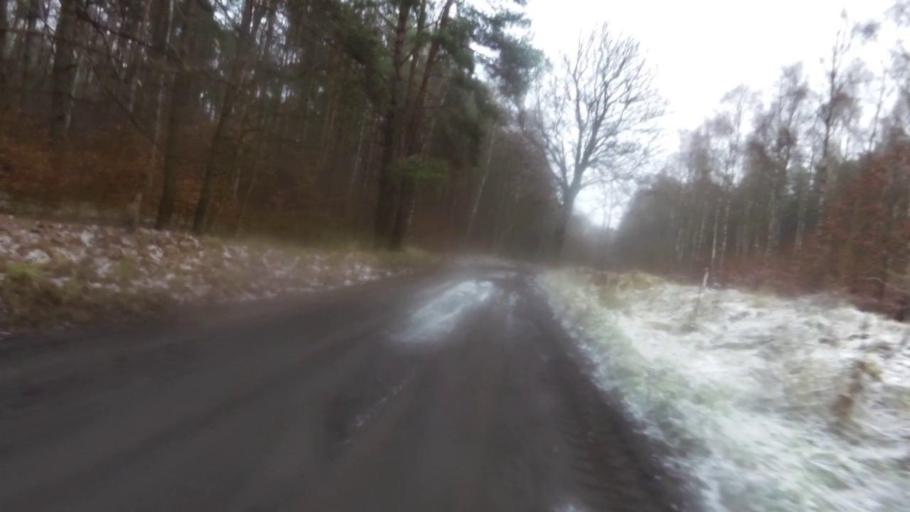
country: PL
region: West Pomeranian Voivodeship
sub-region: Powiat walecki
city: Walcz
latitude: 53.3102
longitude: 16.4494
